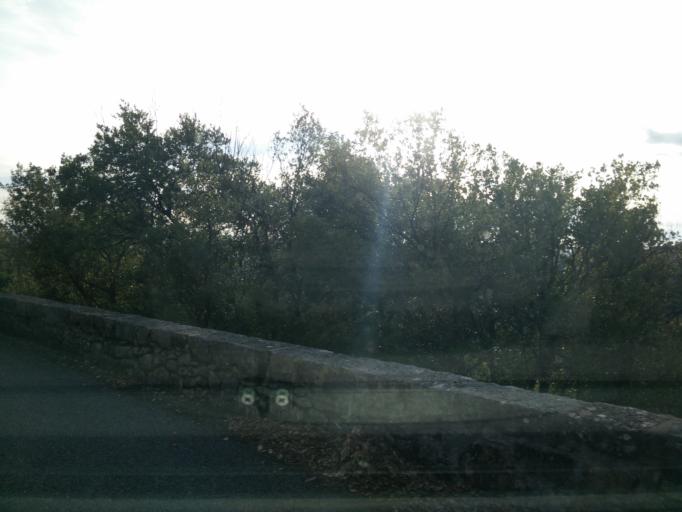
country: FR
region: Provence-Alpes-Cote d'Azur
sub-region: Departement des Alpes-Maritimes
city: Saint-Cezaire-sur-Siagne
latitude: 43.6540
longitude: 6.7898
